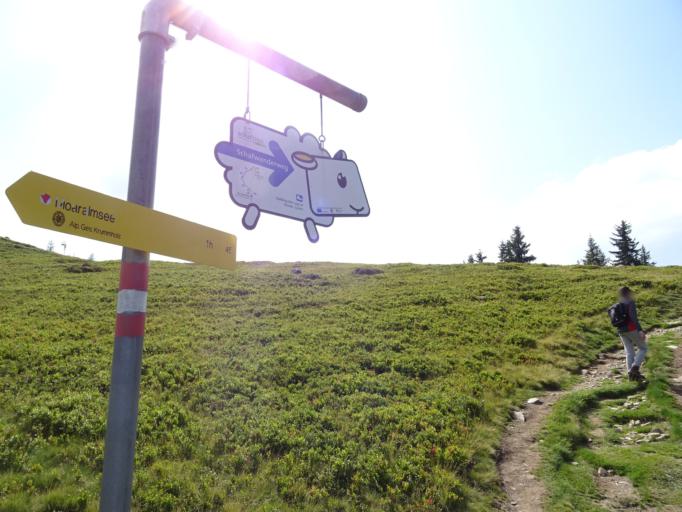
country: AT
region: Styria
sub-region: Politischer Bezirk Liezen
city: Haus
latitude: 47.3649
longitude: 13.7793
